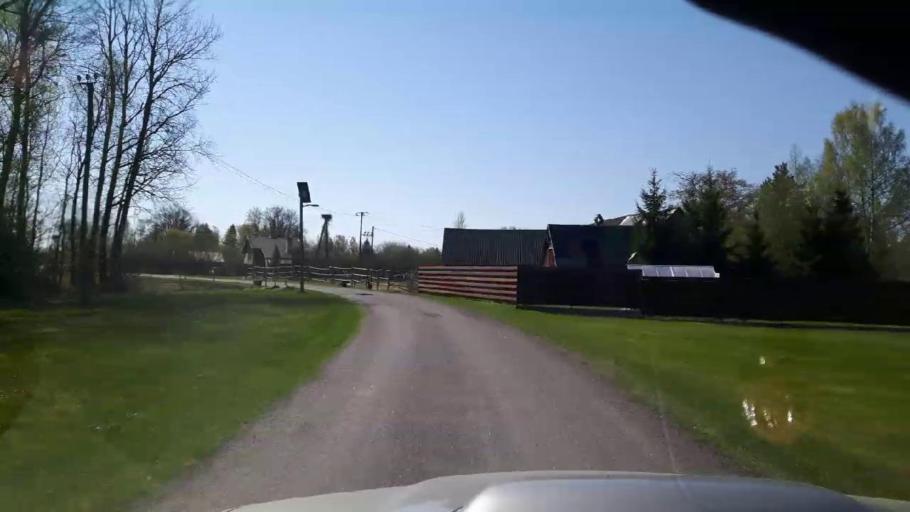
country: EE
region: Paernumaa
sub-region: Tootsi vald
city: Tootsi
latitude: 58.4694
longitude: 24.7881
